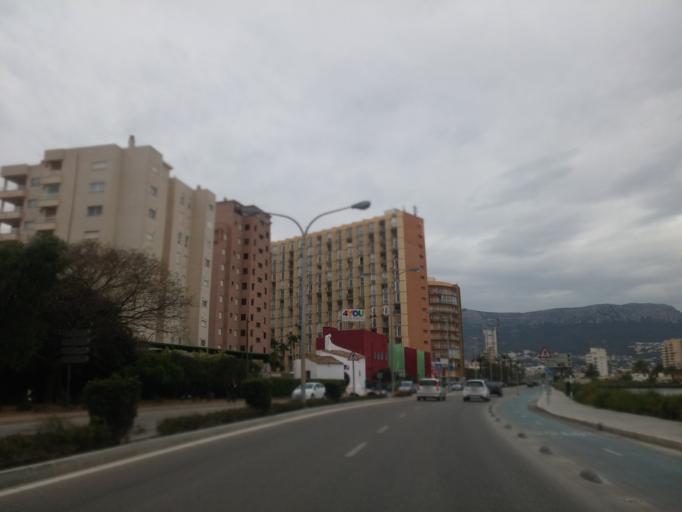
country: ES
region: Valencia
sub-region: Provincia de Alicante
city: Calp
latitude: 38.6420
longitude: 0.0653
